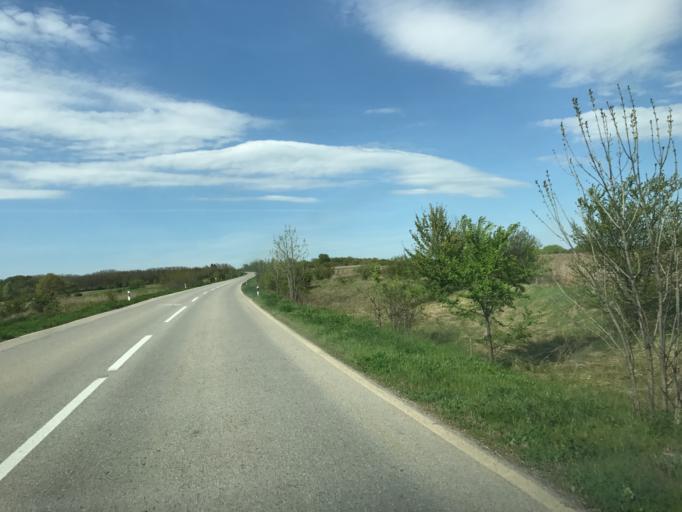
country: RS
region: Central Serbia
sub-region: Zajecarski Okrug
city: Zajecar
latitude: 44.0470
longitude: 22.3344
